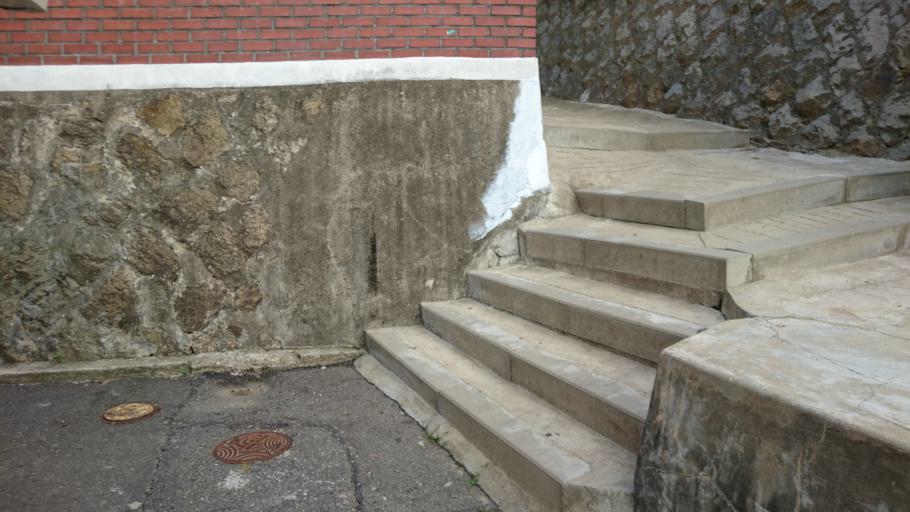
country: KR
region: Seoul
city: Seoul
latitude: 37.5442
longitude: 126.9825
